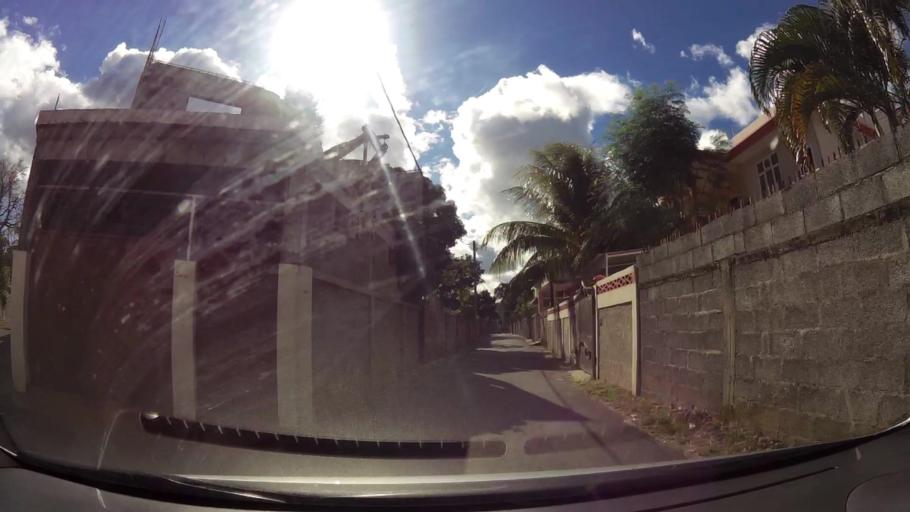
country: MU
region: Pamplemousses
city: Le Hochet
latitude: -20.1486
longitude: 57.5159
